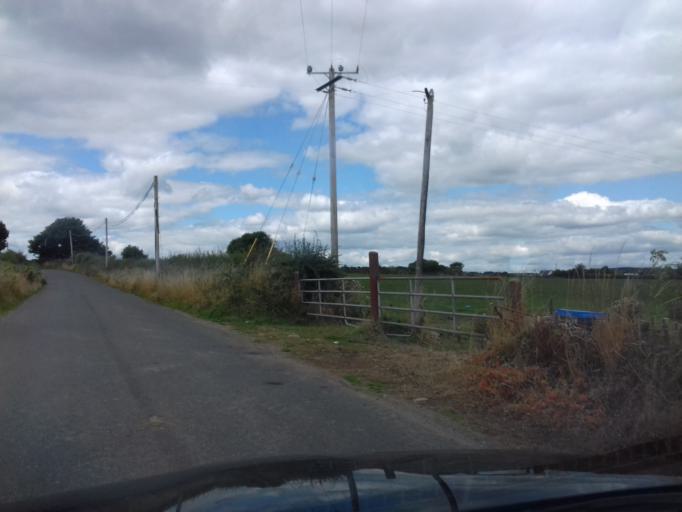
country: IE
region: Munster
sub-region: Waterford
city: Portlaw
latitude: 52.1809
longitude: -7.2953
